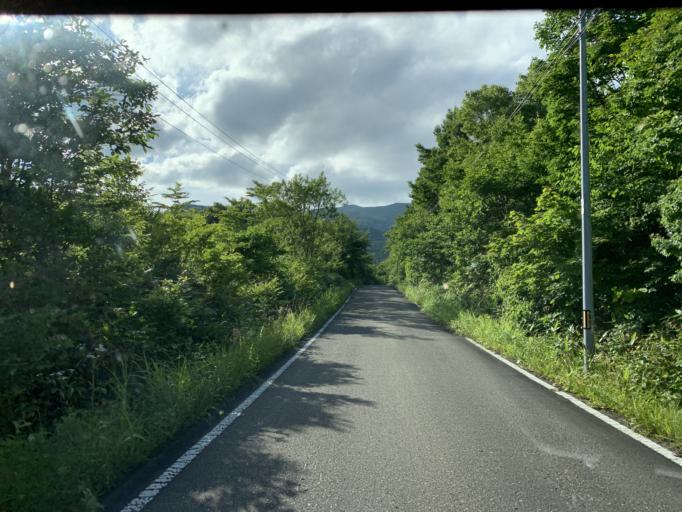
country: JP
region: Iwate
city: Ichinoseki
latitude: 38.9281
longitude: 140.8330
